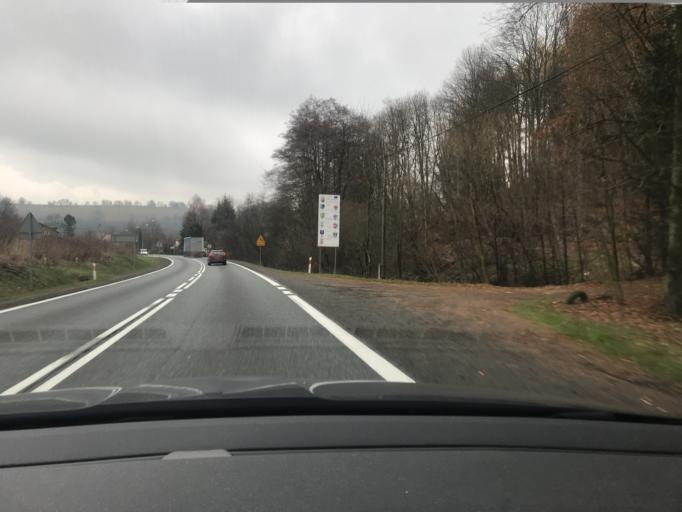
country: PL
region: Lower Silesian Voivodeship
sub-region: Powiat klodzki
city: Duszniki-Zdroj
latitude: 50.4009
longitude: 16.3799
